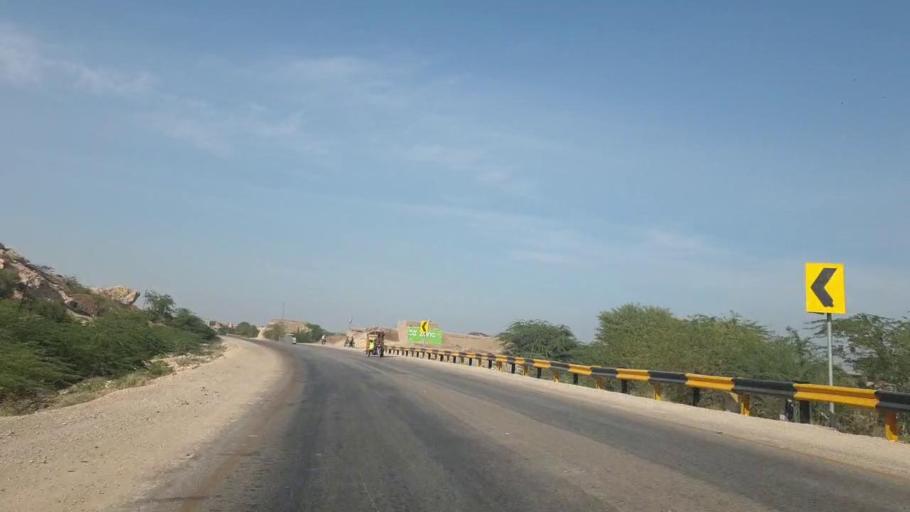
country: PK
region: Sindh
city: Sehwan
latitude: 26.2999
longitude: 67.8950
